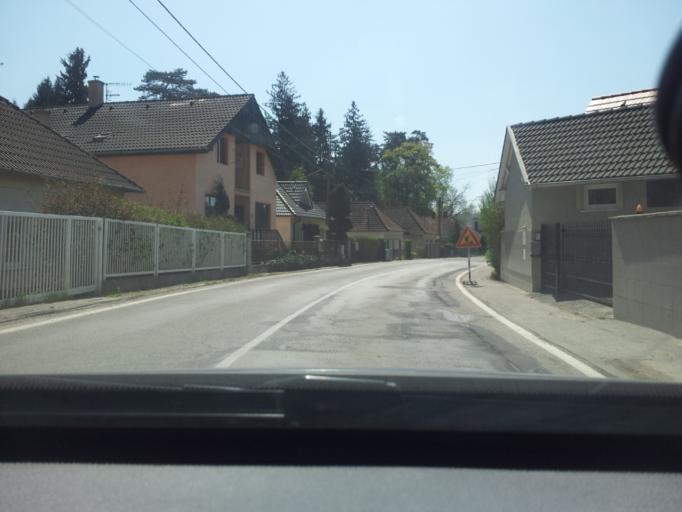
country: SK
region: Nitriansky
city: Zlate Moravce
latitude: 48.4268
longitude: 18.4113
